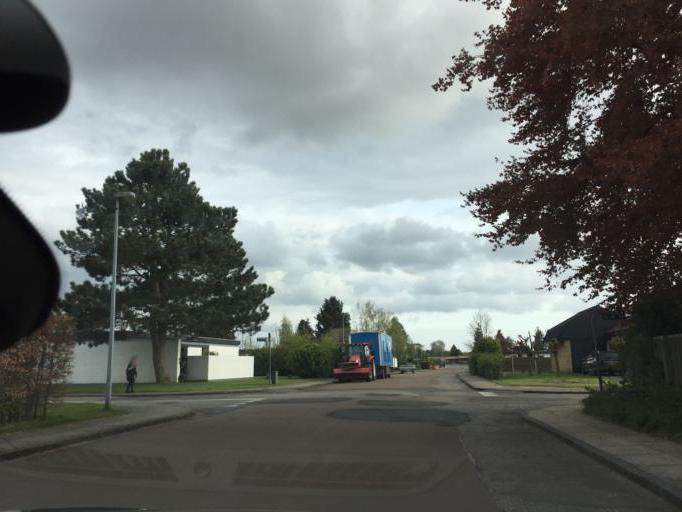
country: DK
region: South Denmark
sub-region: Odense Kommune
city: Odense
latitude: 55.4122
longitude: 10.3415
